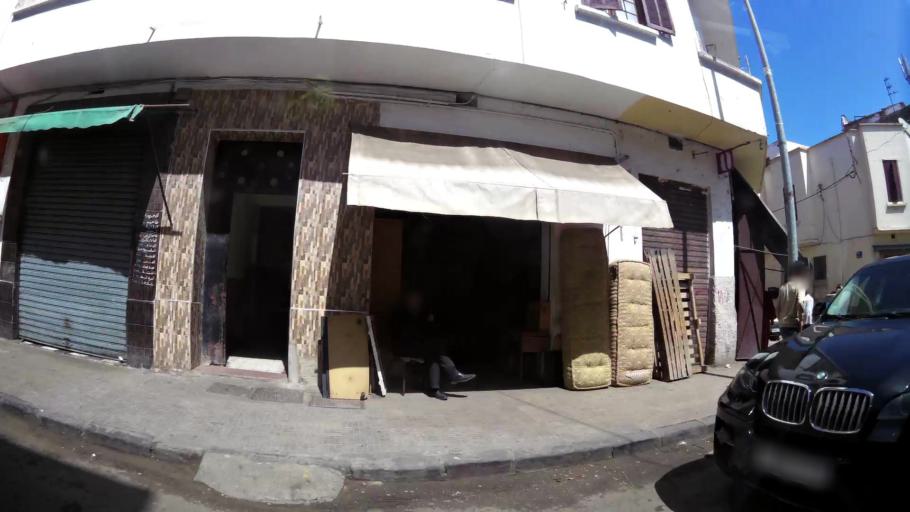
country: MA
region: Grand Casablanca
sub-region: Casablanca
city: Casablanca
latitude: 33.5975
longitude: -7.6263
